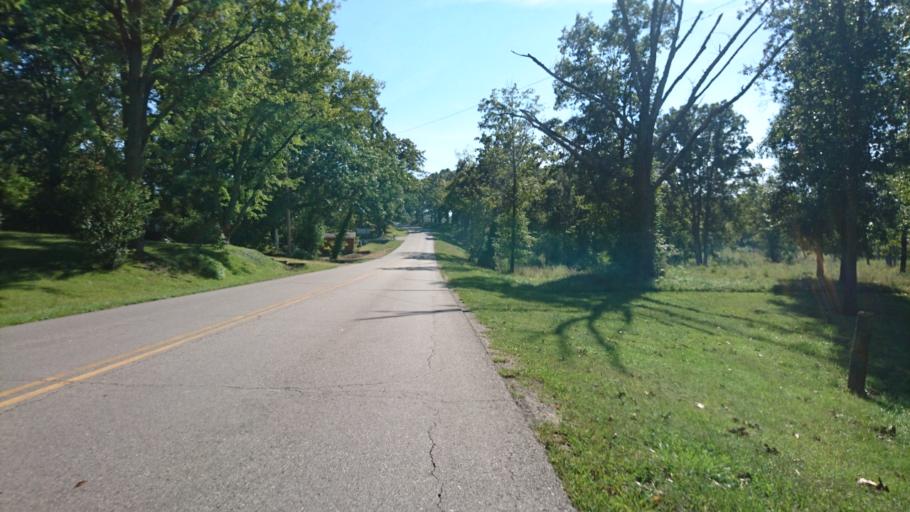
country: US
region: Missouri
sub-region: Crawford County
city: Bourbon
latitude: 38.1557
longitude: -91.2470
